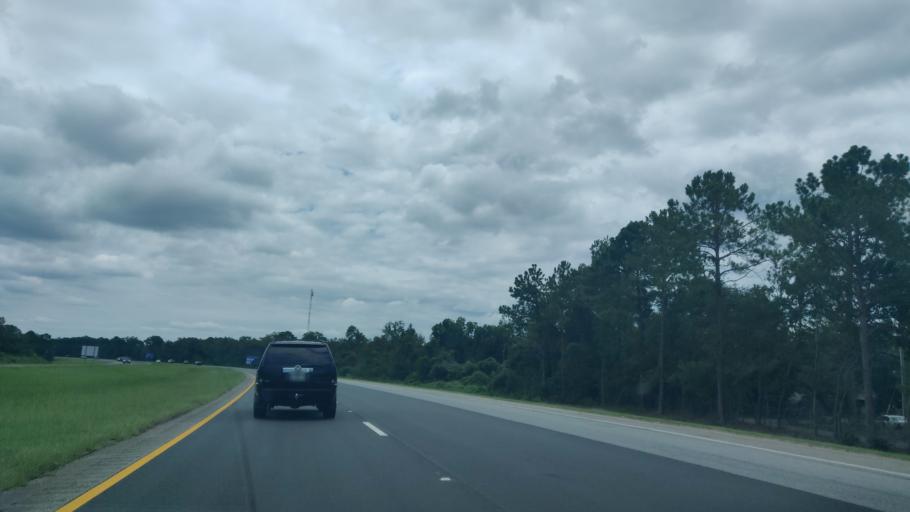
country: US
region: Georgia
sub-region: Dougherty County
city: Albany
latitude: 31.6155
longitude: -84.1979
